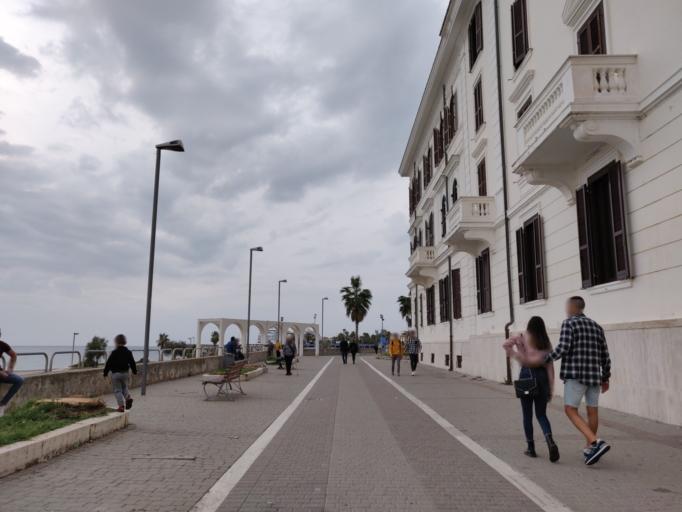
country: IT
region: Latium
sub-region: Citta metropolitana di Roma Capitale
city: Civitavecchia
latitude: 42.0874
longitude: 11.7974
